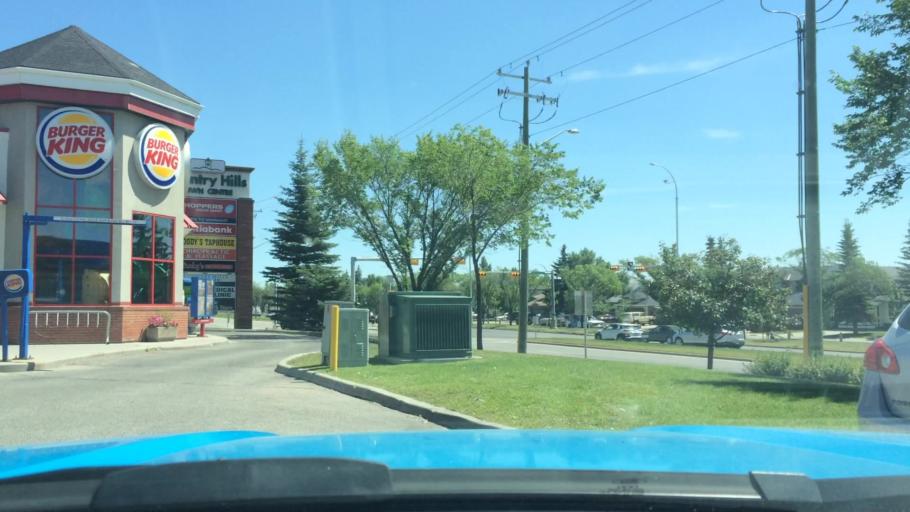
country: CA
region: Alberta
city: Calgary
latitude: 51.1545
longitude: -114.0535
